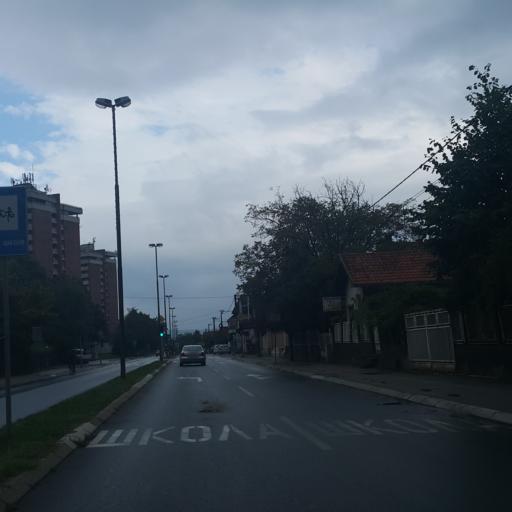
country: RS
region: Central Serbia
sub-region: Rasinski Okrug
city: Krusevac
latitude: 43.5736
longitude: 21.3413
